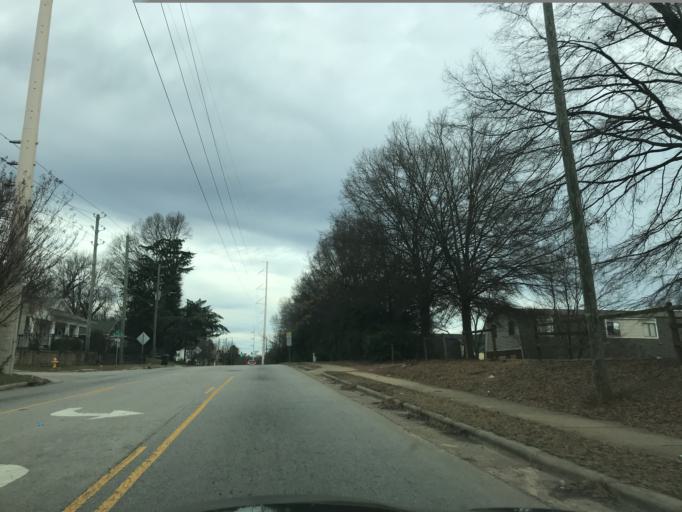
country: US
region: North Carolina
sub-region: Wake County
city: Raleigh
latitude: 35.7641
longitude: -78.6315
